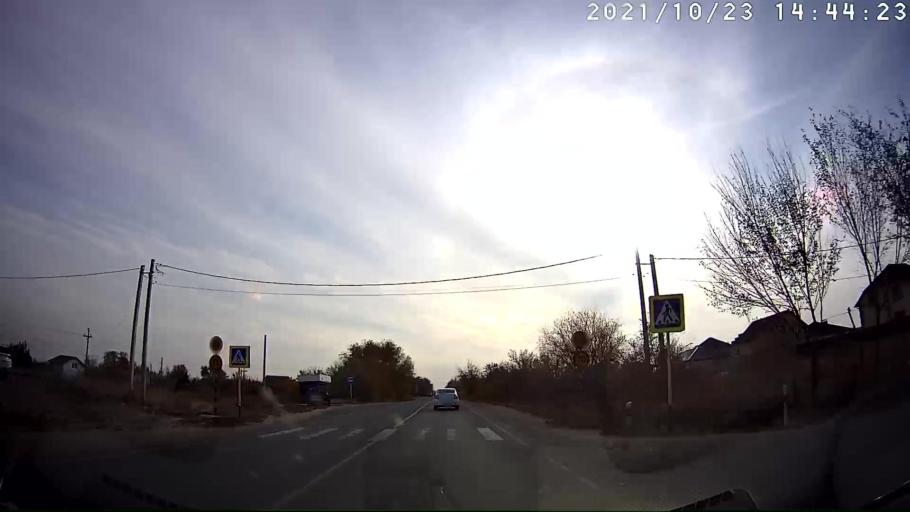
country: RU
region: Volgograd
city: Krasnoslobodsk
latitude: 48.4538
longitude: 44.5184
